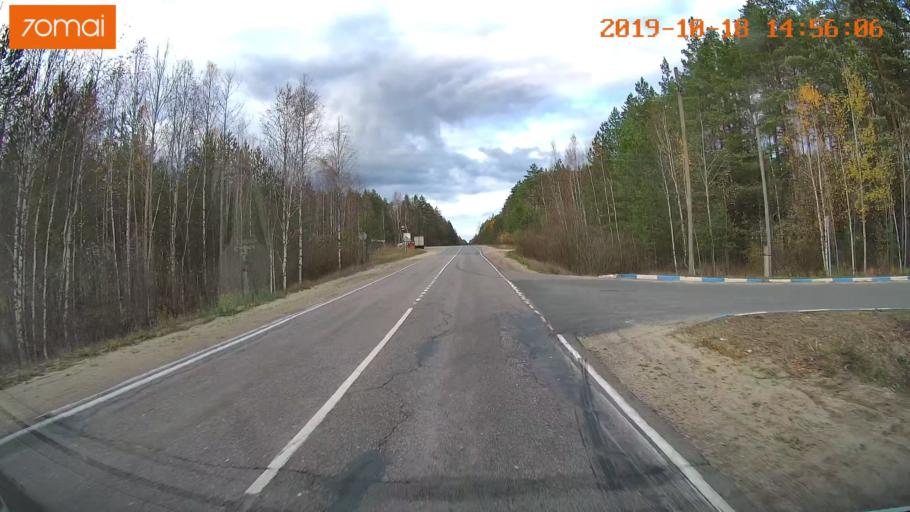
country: RU
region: Vladimir
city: Kurlovo
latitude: 55.4603
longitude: 40.5891
